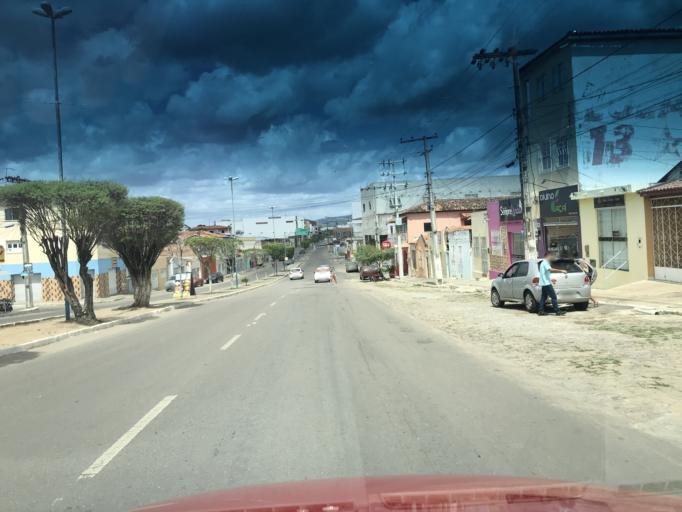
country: BR
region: Bahia
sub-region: Itaberaba
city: Itaberaba
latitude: -12.5269
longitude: -40.3070
